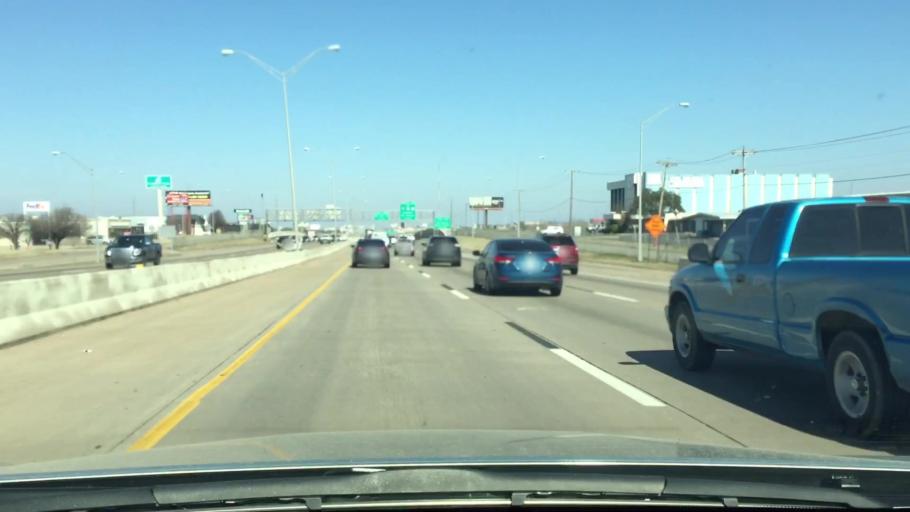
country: US
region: Oklahoma
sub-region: Cleveland County
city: Moore
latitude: 35.3790
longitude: -97.4950
